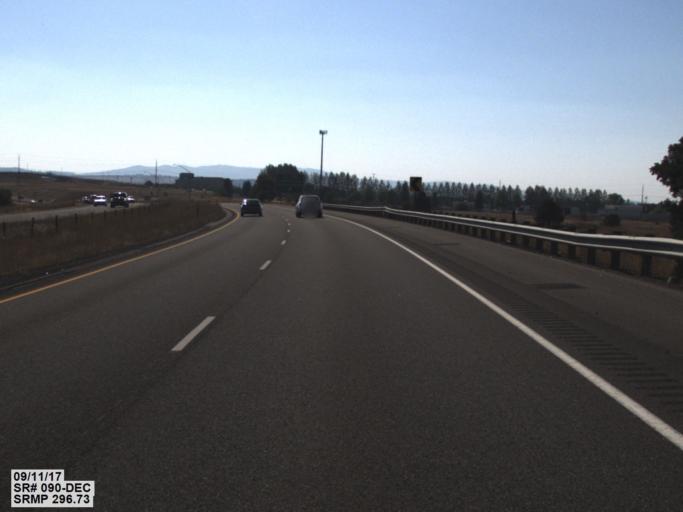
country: US
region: Washington
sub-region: Spokane County
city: Liberty Lake
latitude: 47.6785
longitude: -117.1020
